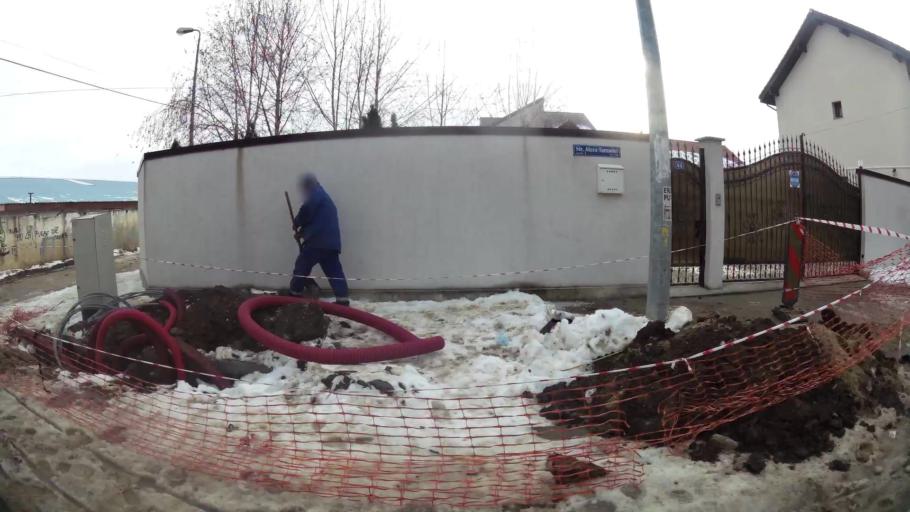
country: RO
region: Ilfov
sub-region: Comuna Popesti-Leordeni
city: Popesti-Leordeni
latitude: 44.4032
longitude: 26.1798
